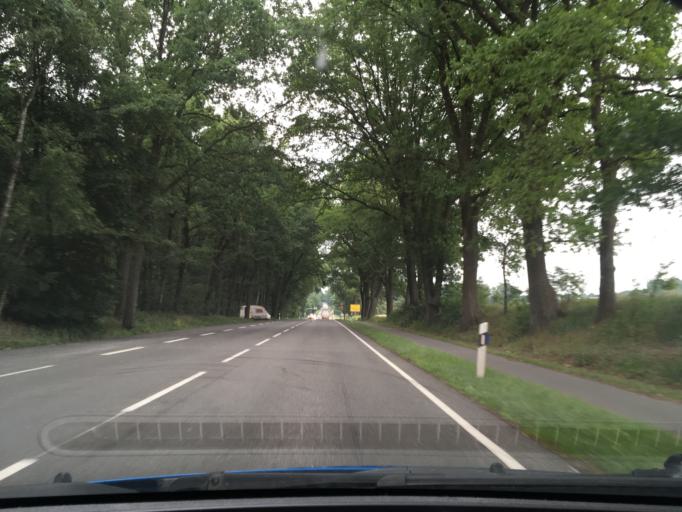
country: DE
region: Lower Saxony
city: Appel
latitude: 53.4031
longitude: 9.7888
